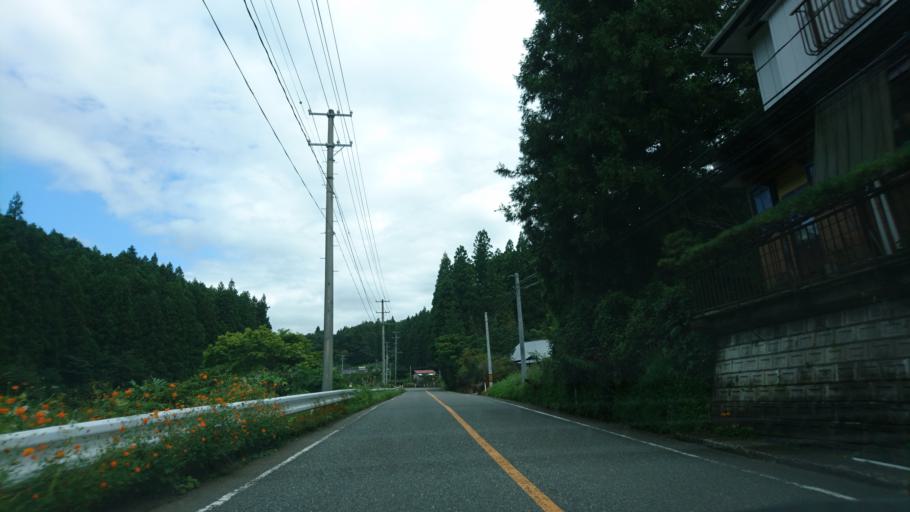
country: JP
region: Miyagi
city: Furukawa
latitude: 38.7698
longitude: 140.8633
